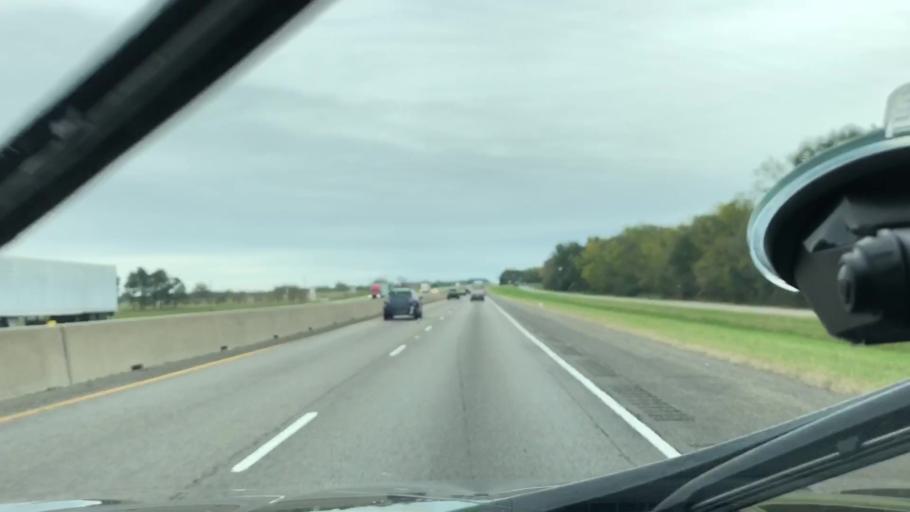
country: US
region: Texas
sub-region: Franklin County
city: Mount Vernon
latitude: 33.1667
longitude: -95.3535
